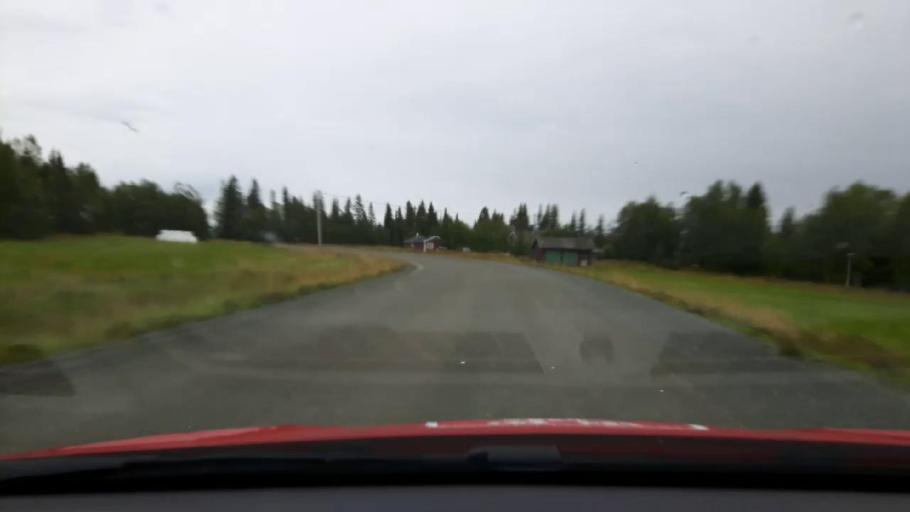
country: SE
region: Jaemtland
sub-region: Are Kommun
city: Are
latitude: 63.4707
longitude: 12.5763
